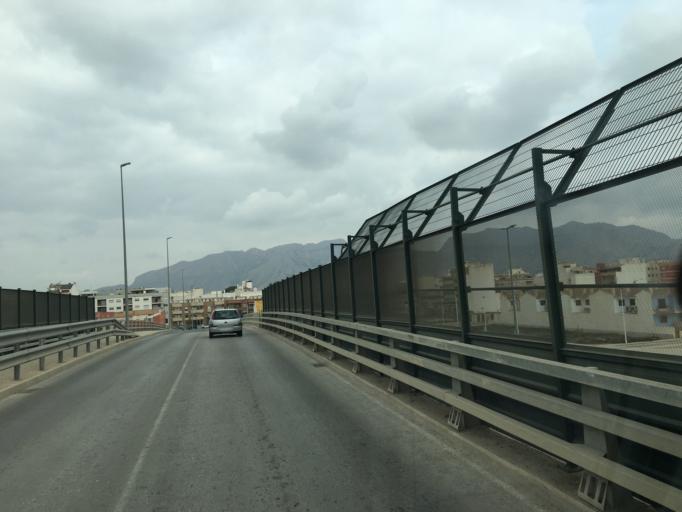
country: ES
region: Murcia
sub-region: Murcia
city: Beniel
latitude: 38.0460
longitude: -0.9969
